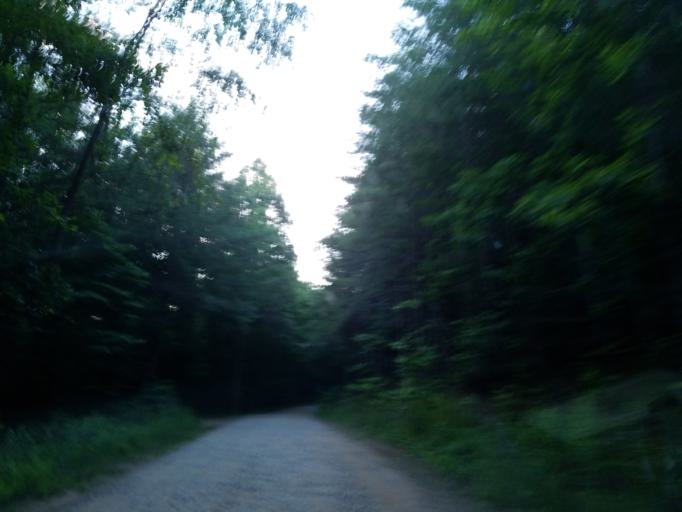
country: US
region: Georgia
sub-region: Fannin County
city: Blue Ridge
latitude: 34.7492
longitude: -84.1782
